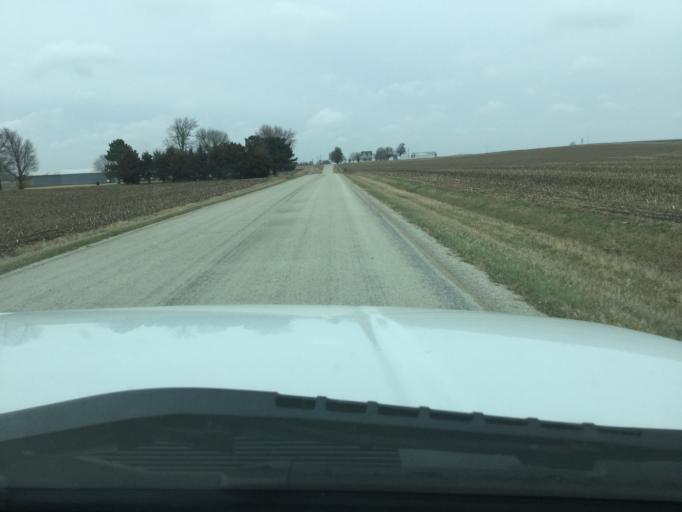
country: US
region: Kansas
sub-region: Nemaha County
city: Sabetha
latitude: 39.8464
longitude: -95.7142
